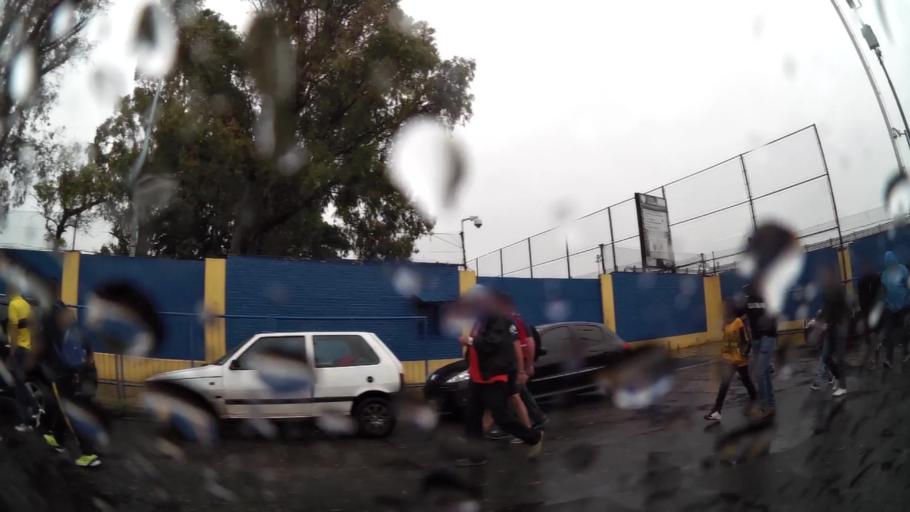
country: AR
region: Buenos Aires F.D.
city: Buenos Aires
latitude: -34.6338
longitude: -58.3652
